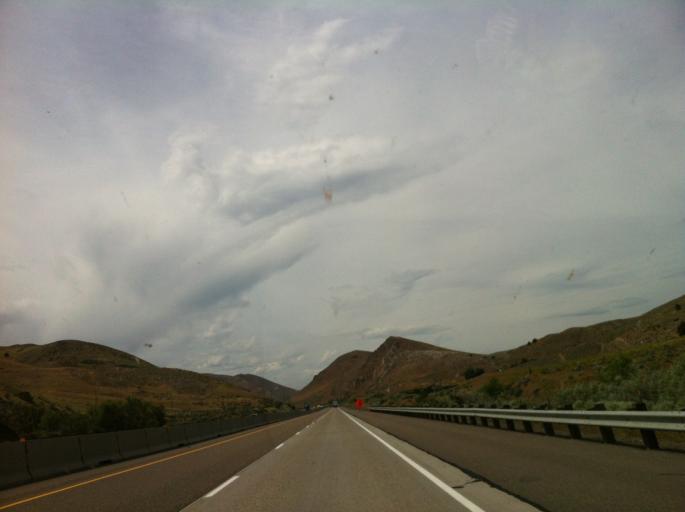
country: US
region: Idaho
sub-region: Washington County
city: Weiser
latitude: 44.3809
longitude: -117.3033
